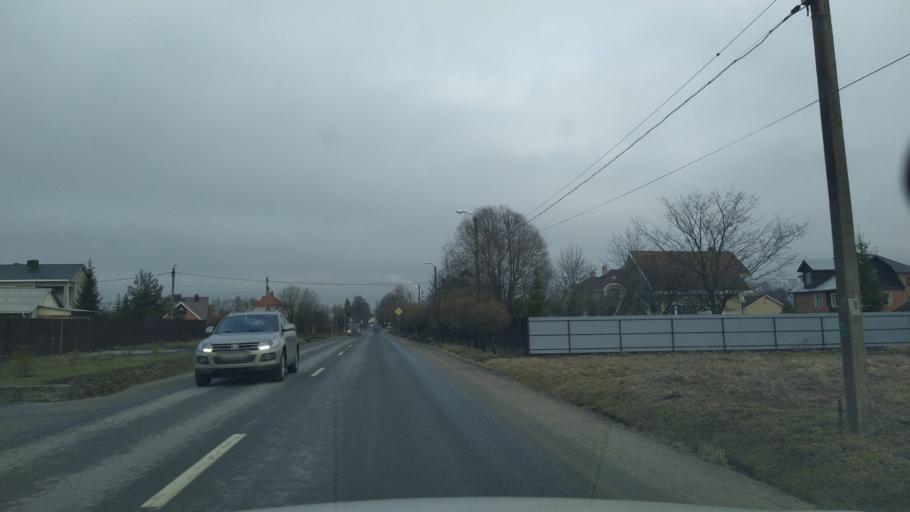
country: RU
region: St.-Petersburg
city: Aleksandrovskaya
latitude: 59.7237
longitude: 30.3484
